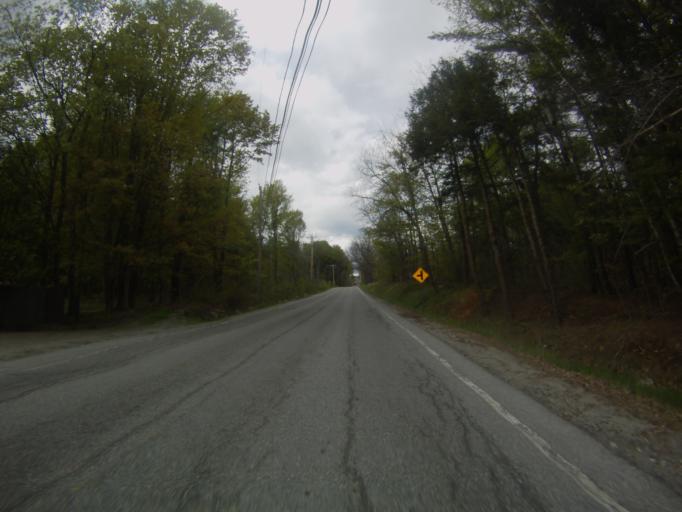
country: US
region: New York
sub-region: Essex County
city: Mineville
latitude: 44.0759
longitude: -73.5272
